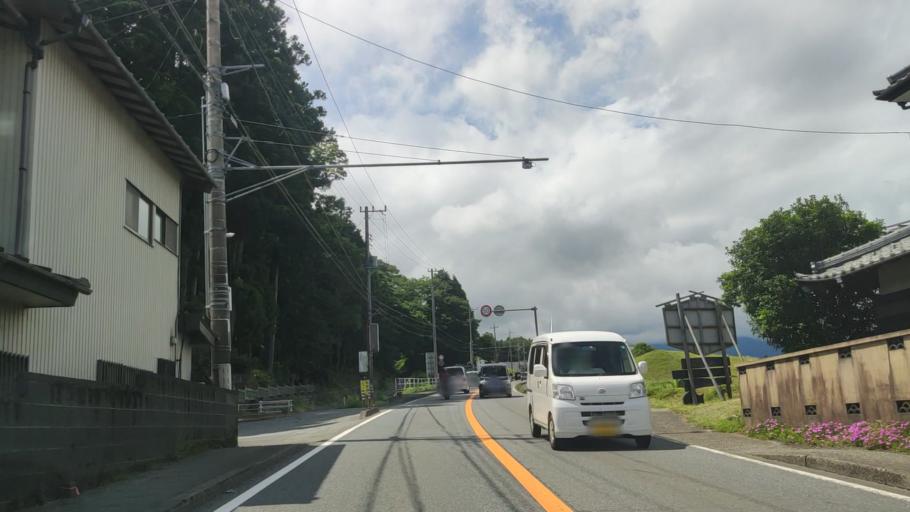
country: JP
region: Shizuoka
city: Gotemba
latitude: 35.3250
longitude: 138.9083
